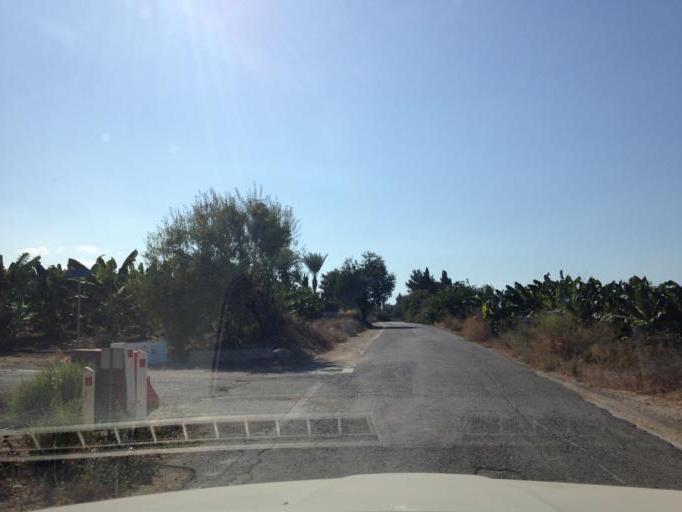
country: CY
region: Pafos
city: Pegeia
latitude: 34.8634
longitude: 32.3631
